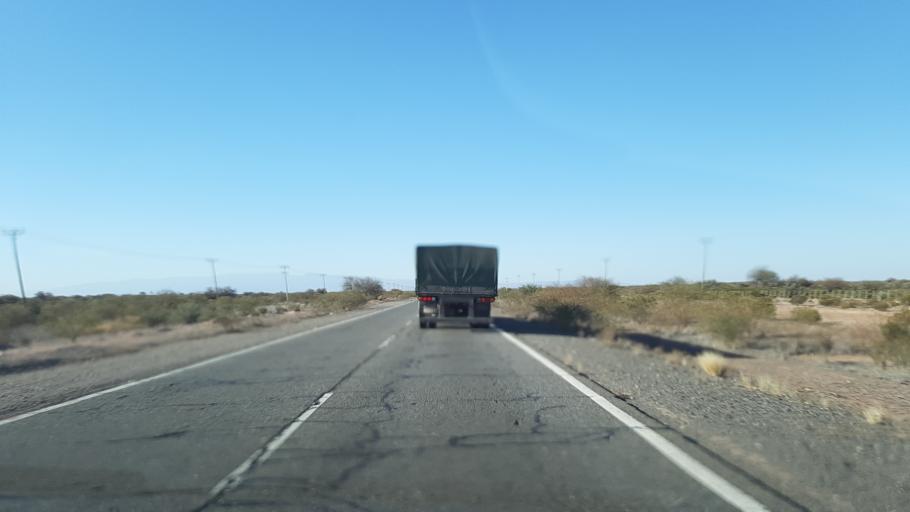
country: AR
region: San Juan
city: Caucete
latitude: -31.6494
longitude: -67.7638
